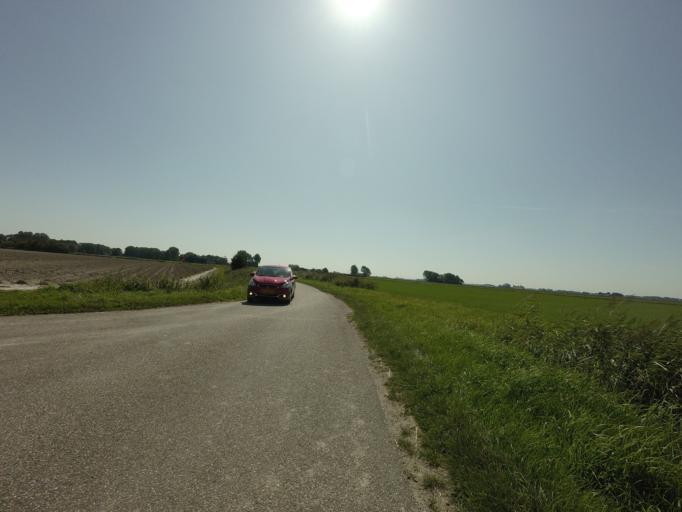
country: NL
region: Friesland
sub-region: Gemeente Dongeradeel
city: Ternaard
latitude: 53.3837
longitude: 6.0285
